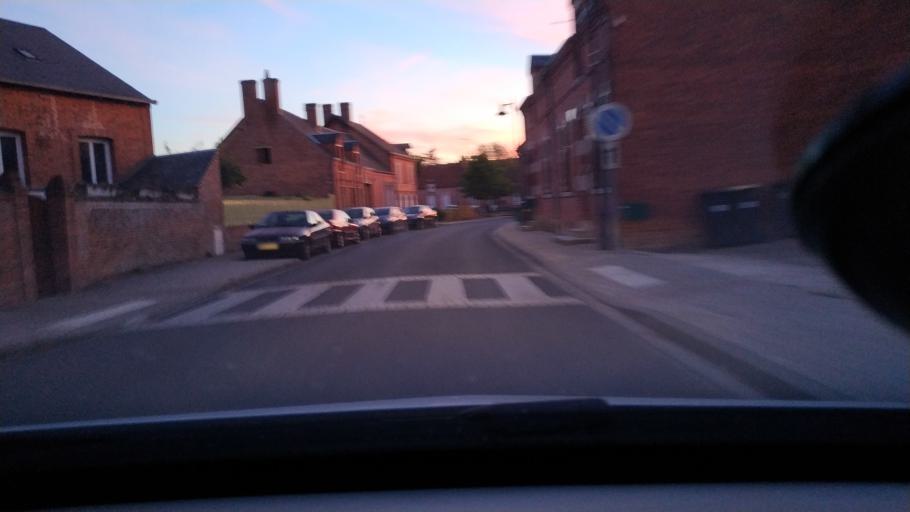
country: FR
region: Centre
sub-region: Departement du Cher
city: Brinon-sur-Sauldre
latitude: 47.6092
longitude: 2.1754
